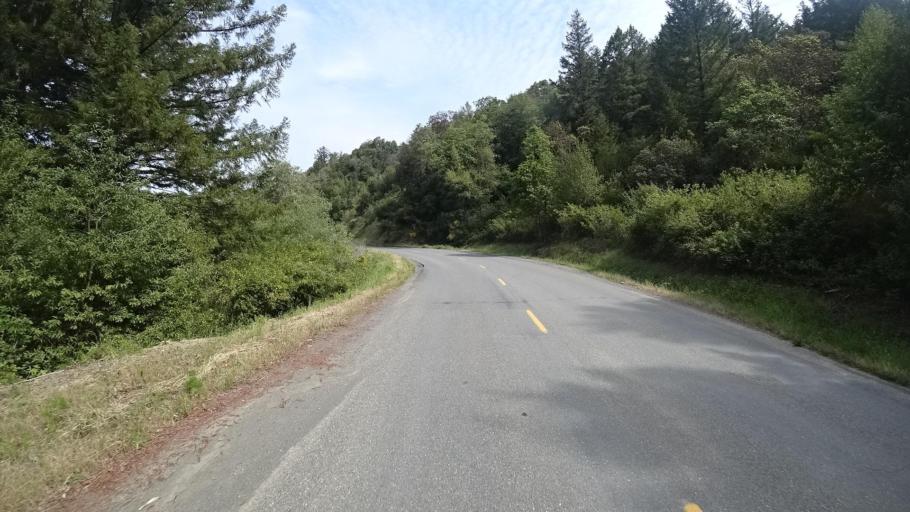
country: US
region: California
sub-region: Humboldt County
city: Redway
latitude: 40.0912
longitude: -123.7944
